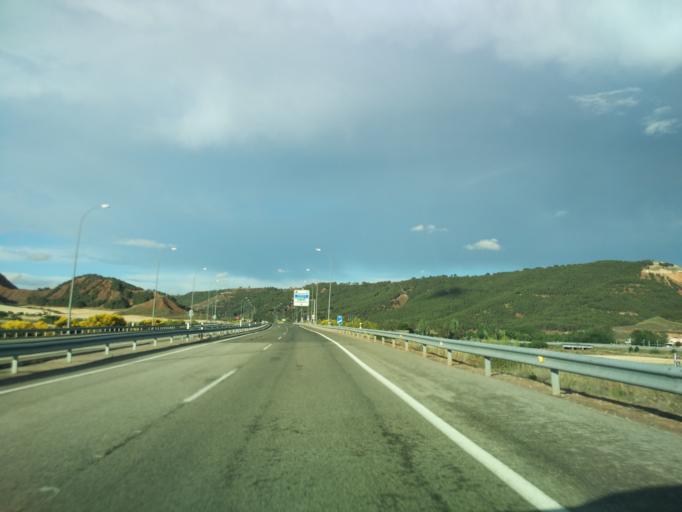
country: ES
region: Castille-La Mancha
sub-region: Provincia de Guadalajara
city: Tortola de Henares
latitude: 40.6598
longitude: -3.1261
